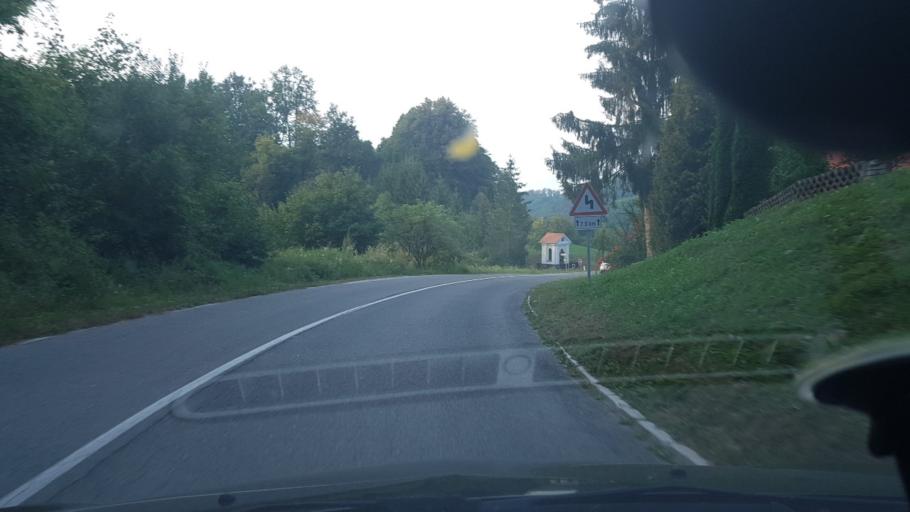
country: SI
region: Kozje
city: Kozje
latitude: 46.0747
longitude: 15.5691
